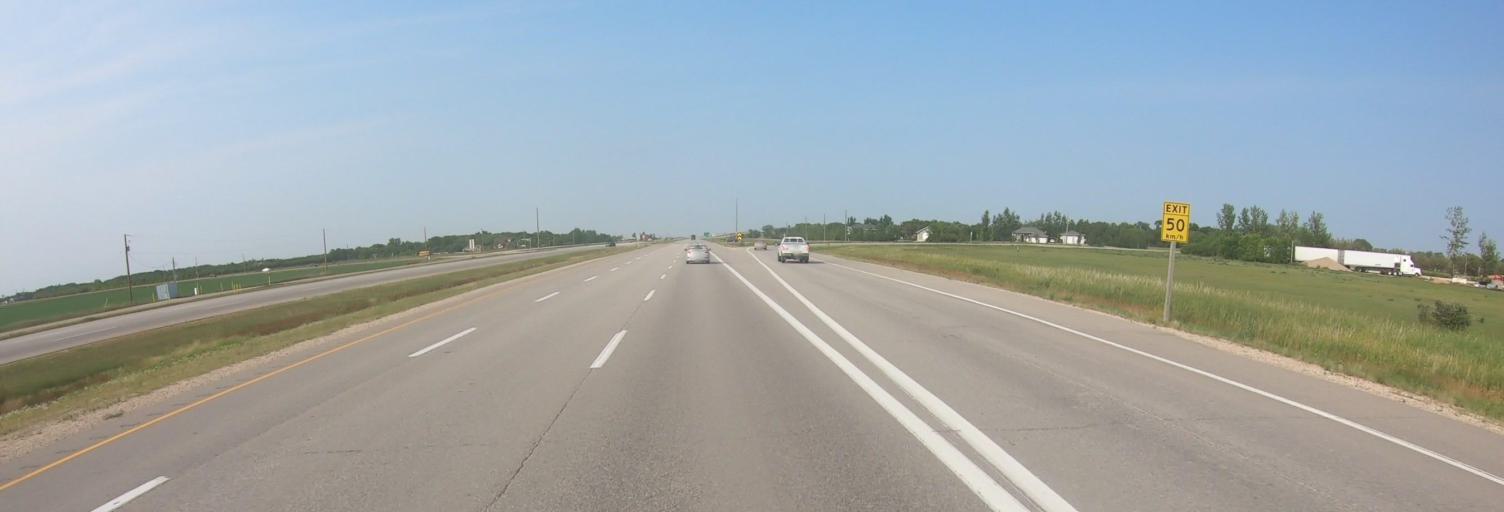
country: CA
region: Manitoba
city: Steinbach
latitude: 49.6634
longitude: -96.6679
